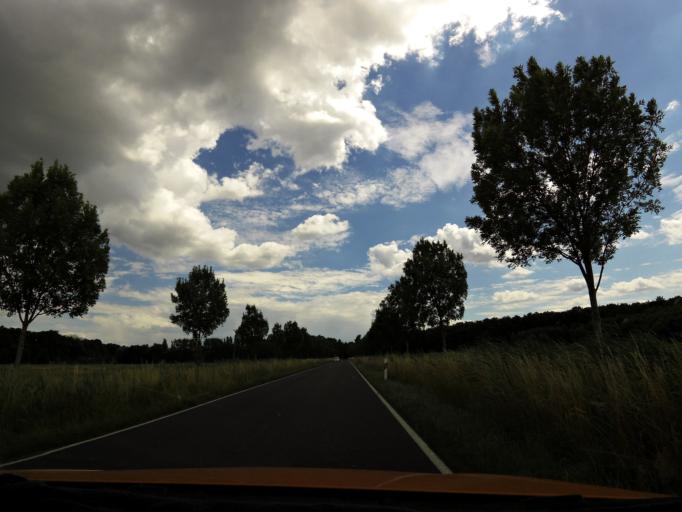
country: DE
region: Brandenburg
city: Munchehofe
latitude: 52.2481
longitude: 13.7960
